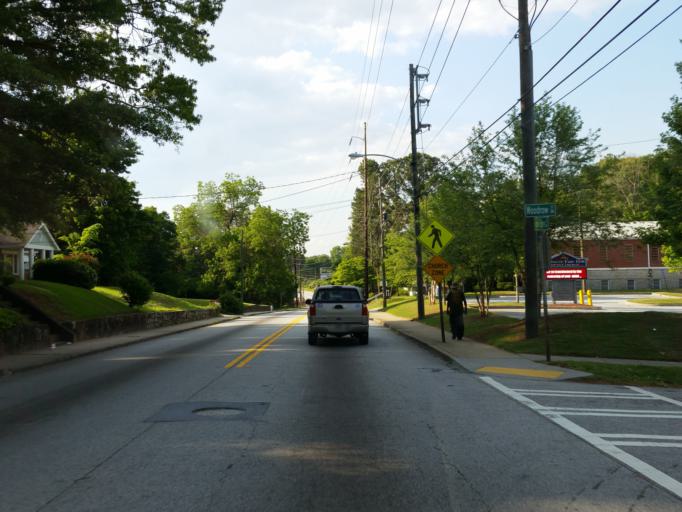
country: US
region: Georgia
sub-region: Fulton County
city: Atlanta
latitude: 33.7738
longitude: -84.4736
